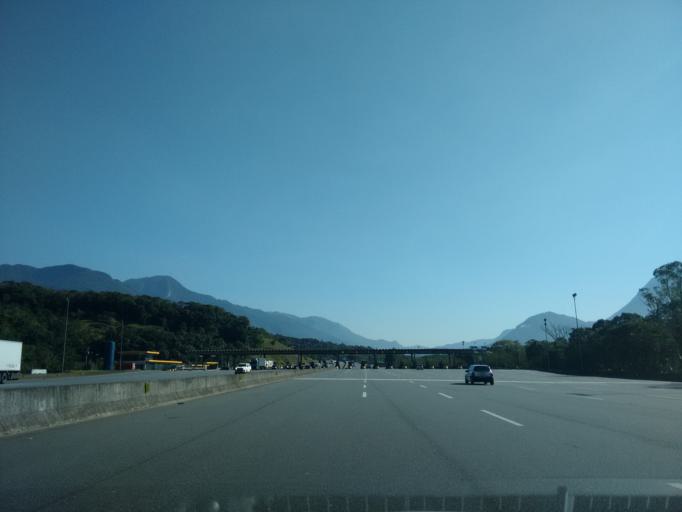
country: BR
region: Santa Catarina
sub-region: Joinville
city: Joinville
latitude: -25.9935
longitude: -48.8803
